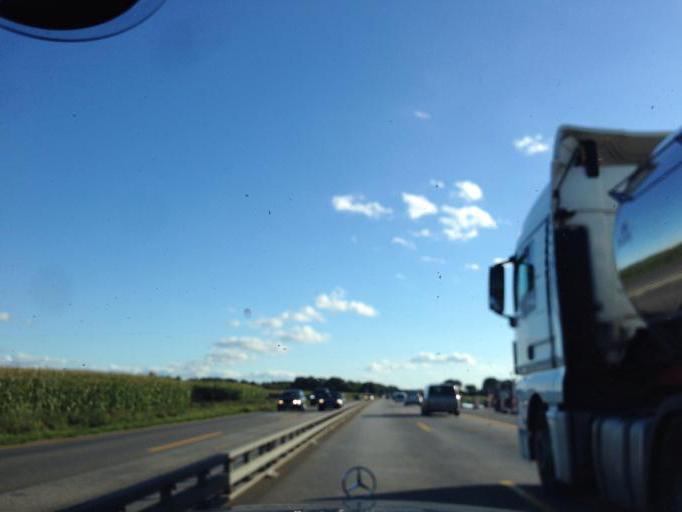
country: DE
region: Schleswig-Holstein
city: Loop
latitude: 54.1520
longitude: 9.9645
